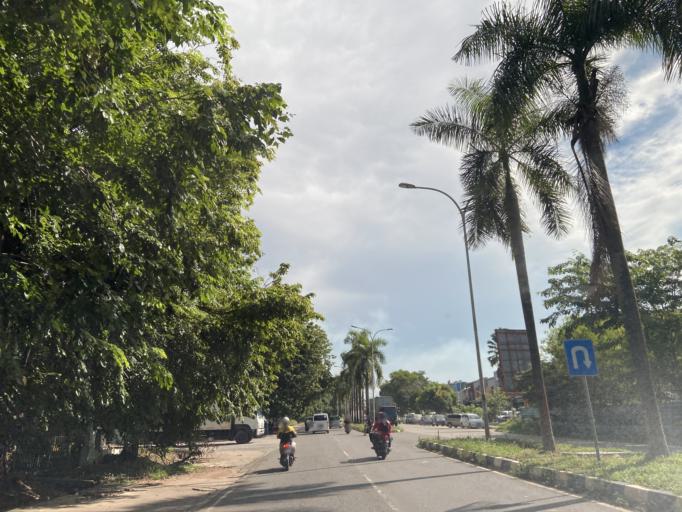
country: SG
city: Singapore
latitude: 1.1156
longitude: 104.0552
